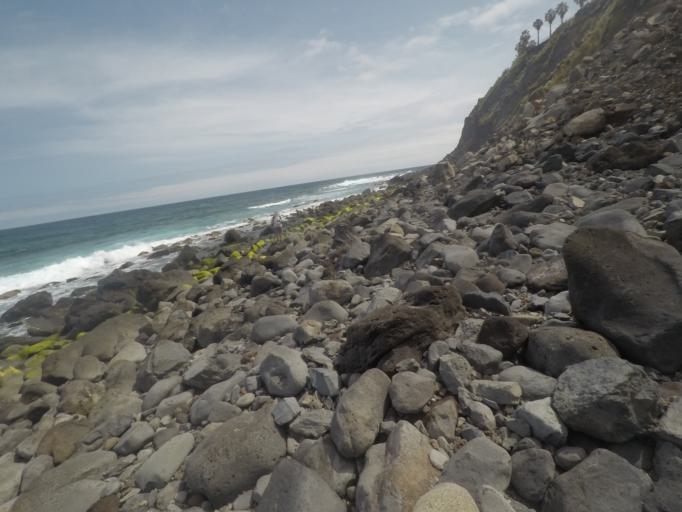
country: PT
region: Madeira
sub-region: Sao Vicente
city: Sao Vicente
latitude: 32.8282
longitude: -16.9932
